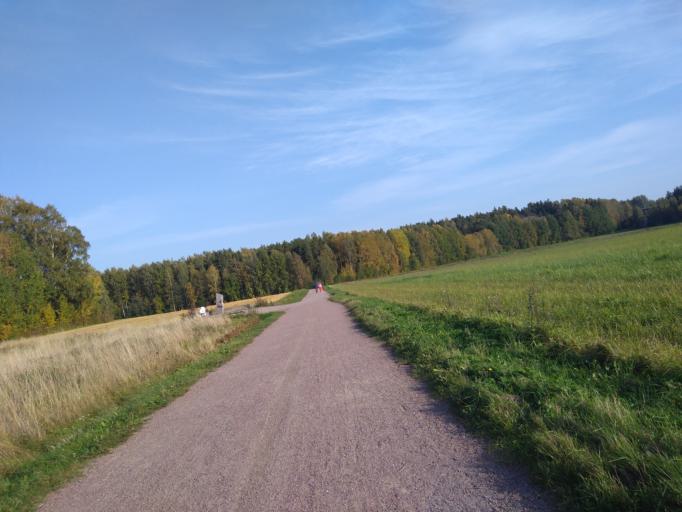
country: FI
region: Uusimaa
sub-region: Helsinki
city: Vantaa
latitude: 60.2239
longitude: 25.0348
